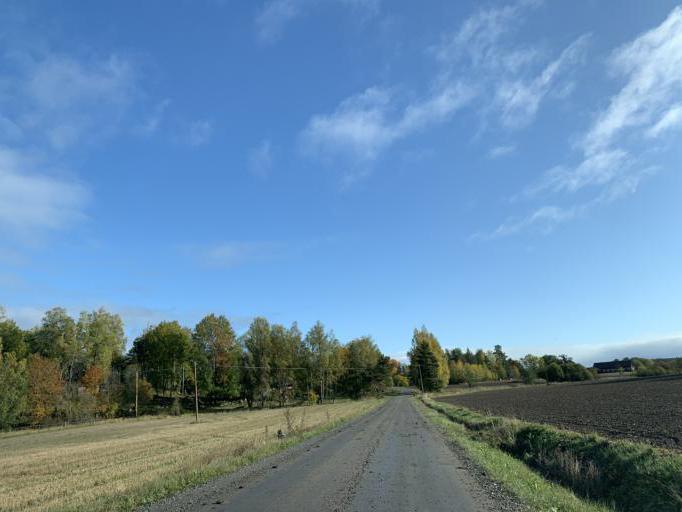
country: SE
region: Soedermanland
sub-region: Eskilstuna Kommun
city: Kvicksund
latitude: 59.3845
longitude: 16.2410
